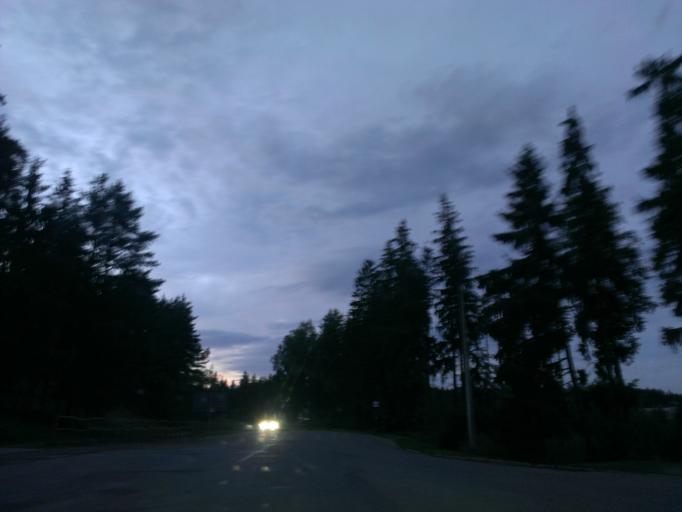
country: LV
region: Ogre
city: Ogre
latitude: 56.8250
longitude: 24.5990
